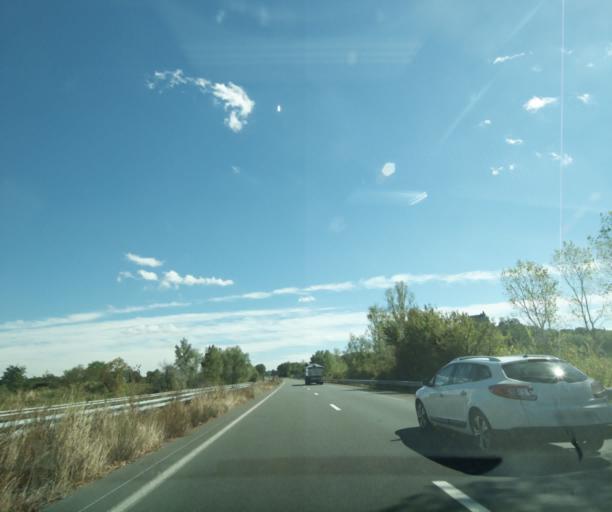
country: FR
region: Aquitaine
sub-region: Departement du Lot-et-Garonne
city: Buzet-sur-Baise
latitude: 44.2557
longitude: 0.2916
